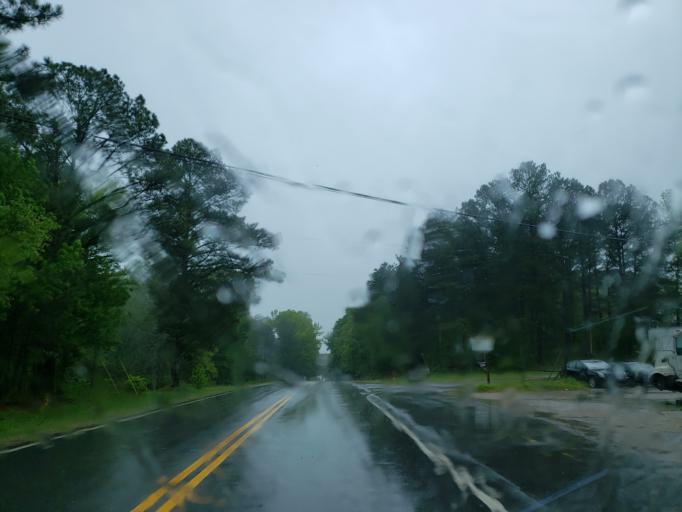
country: US
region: Georgia
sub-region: Haralson County
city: Bremen
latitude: 33.7221
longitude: -85.1022
